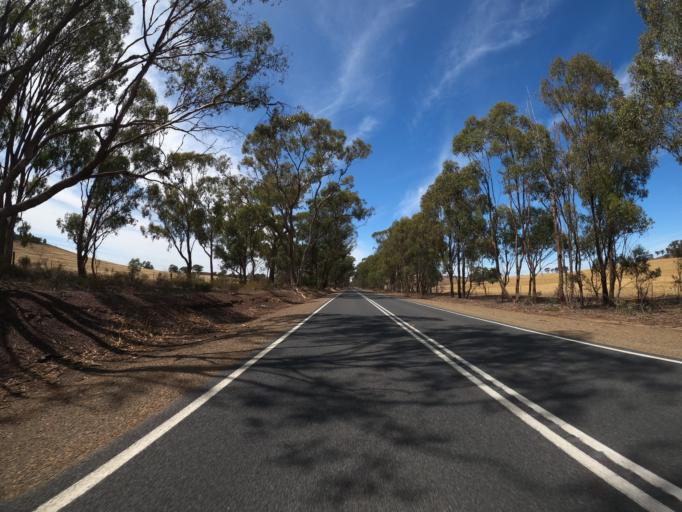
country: AU
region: Victoria
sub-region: Benalla
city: Benalla
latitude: -36.3731
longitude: 145.9735
